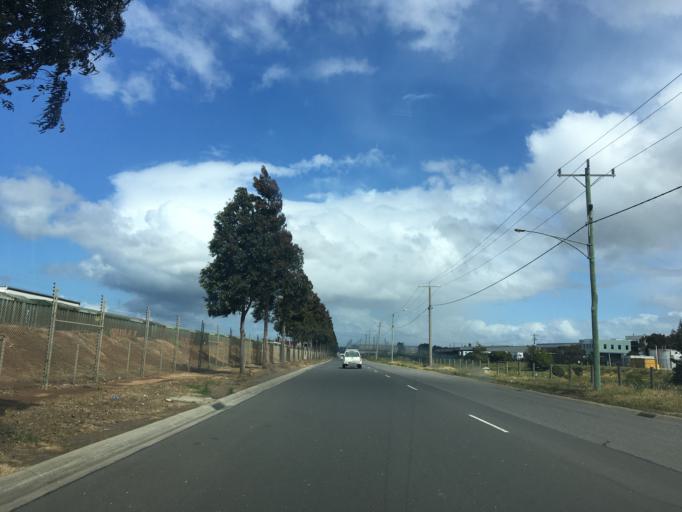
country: AU
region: Victoria
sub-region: Brimbank
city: Sunshine West
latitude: -37.8166
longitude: 144.7980
